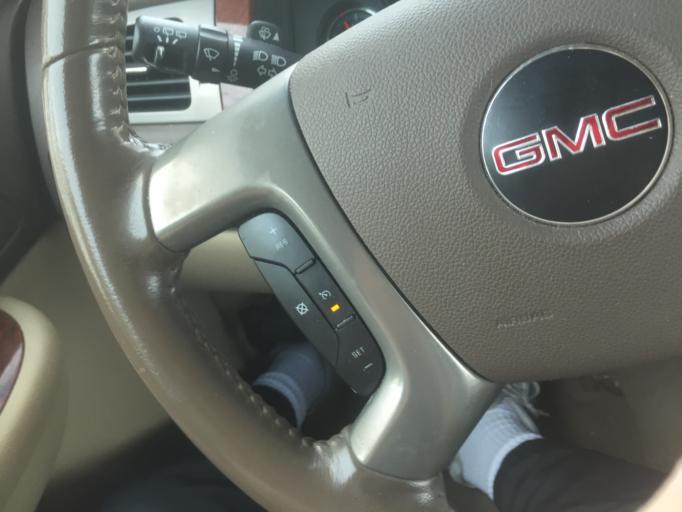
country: US
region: Louisiana
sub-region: Orleans Parish
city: New Orleans
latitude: 29.9975
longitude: -90.0772
